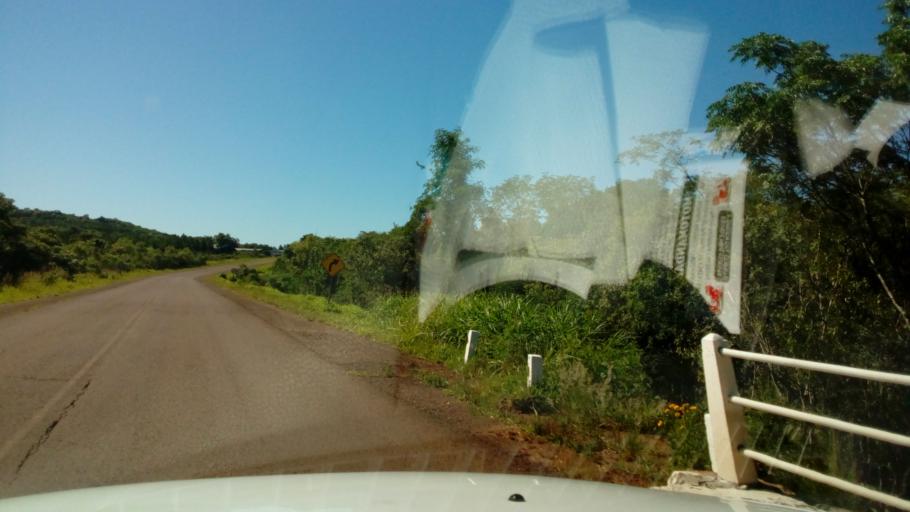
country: AR
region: Misiones
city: Almafuerte
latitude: -27.5317
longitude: -55.4406
